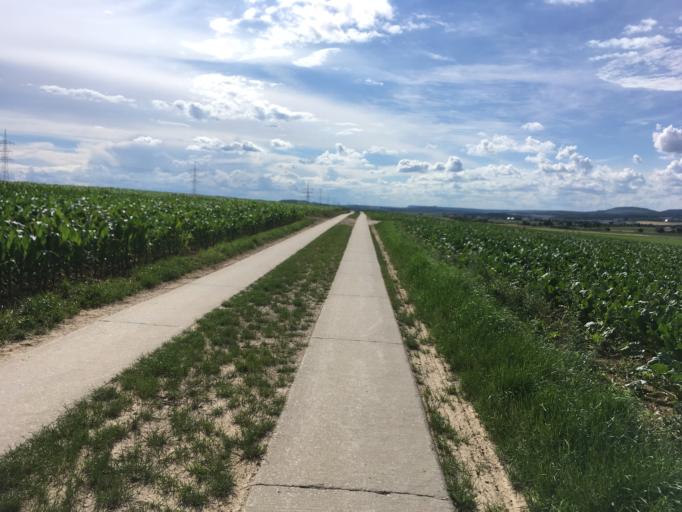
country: DE
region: Baden-Wuerttemberg
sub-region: Regierungsbezirk Stuttgart
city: Oberriexingen
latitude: 48.9402
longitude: 8.9985
